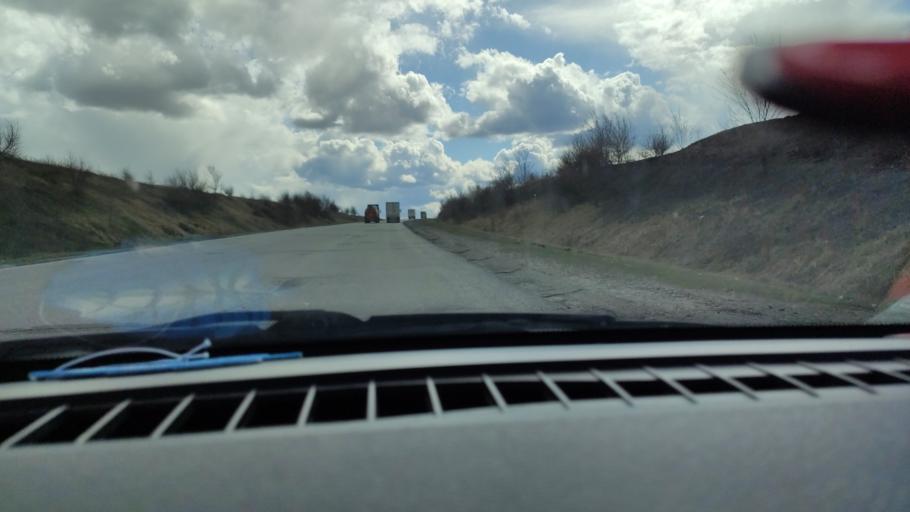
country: RU
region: Samara
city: Varlamovo
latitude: 53.0616
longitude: 48.3518
